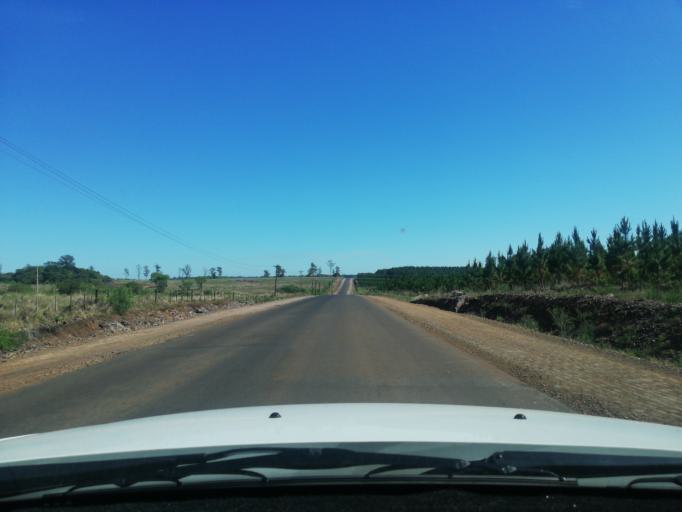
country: AR
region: Misiones
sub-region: Departamento de Candelaria
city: Candelaria
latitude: -27.5081
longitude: -55.7364
